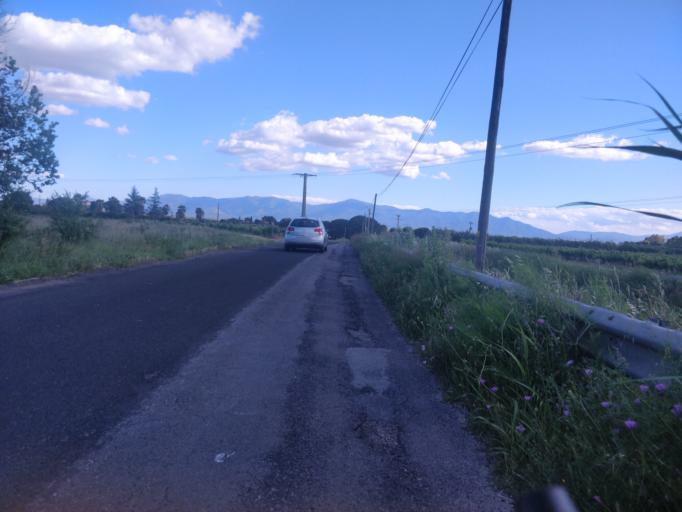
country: FR
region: Languedoc-Roussillon
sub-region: Departement des Pyrenees-Orientales
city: Cabestany
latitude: 42.6762
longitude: 2.9218
